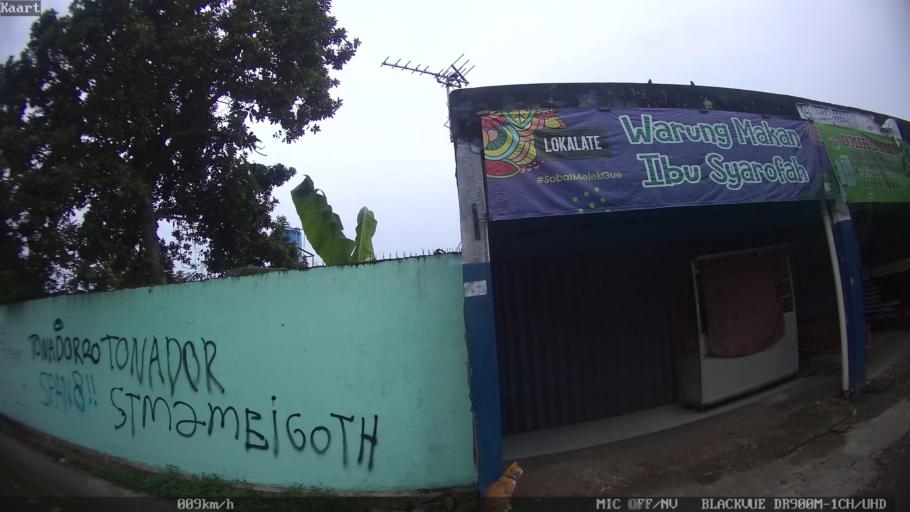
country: ID
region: Lampung
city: Kedaton
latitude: -5.3819
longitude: 105.2464
